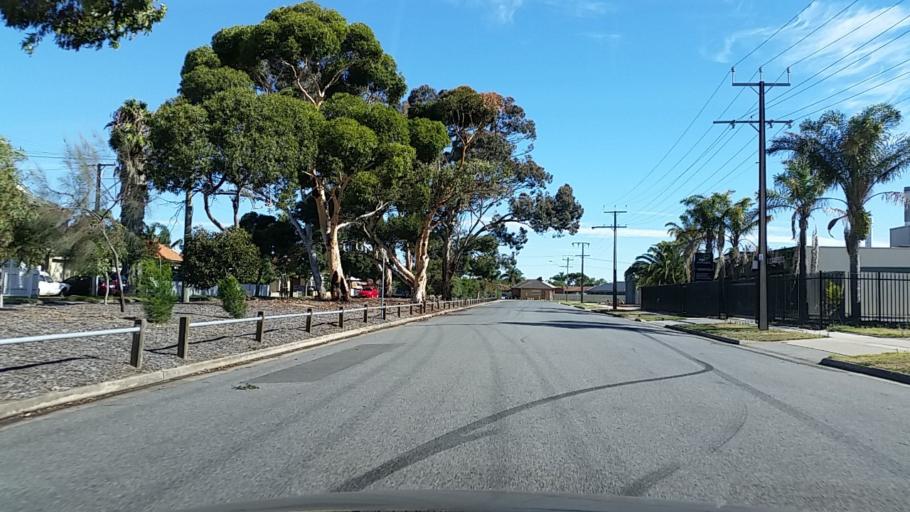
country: AU
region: South Australia
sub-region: Charles Sturt
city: Royal Park
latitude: -34.8668
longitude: 138.5074
